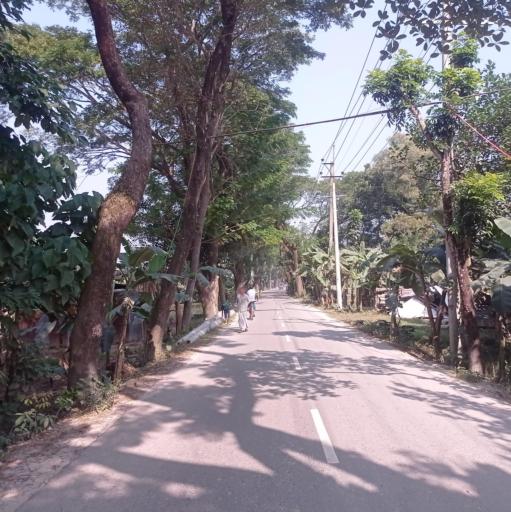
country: BD
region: Dhaka
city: Narsingdi
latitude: 24.0512
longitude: 90.6821
